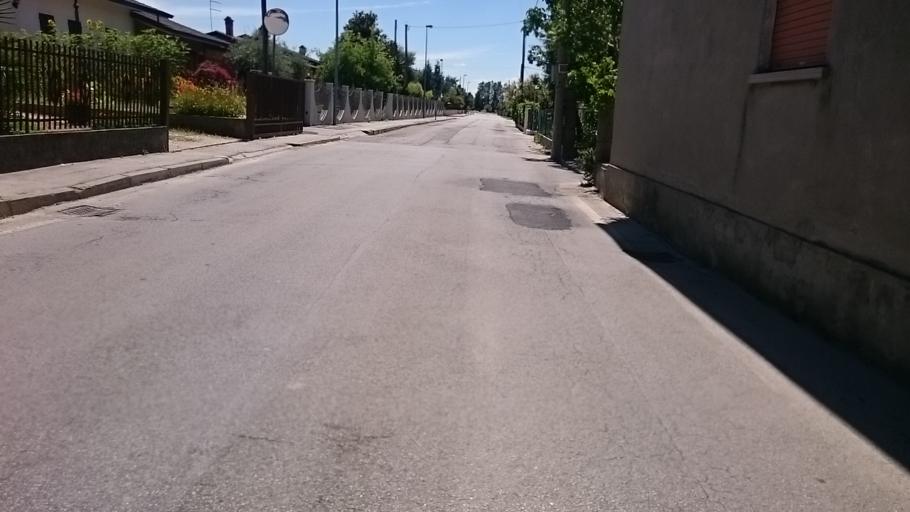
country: IT
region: Veneto
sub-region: Provincia di Padova
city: Borgoricco-San Michele delle Badesse-Sant'Eufemia
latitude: 45.5350
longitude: 11.9381
